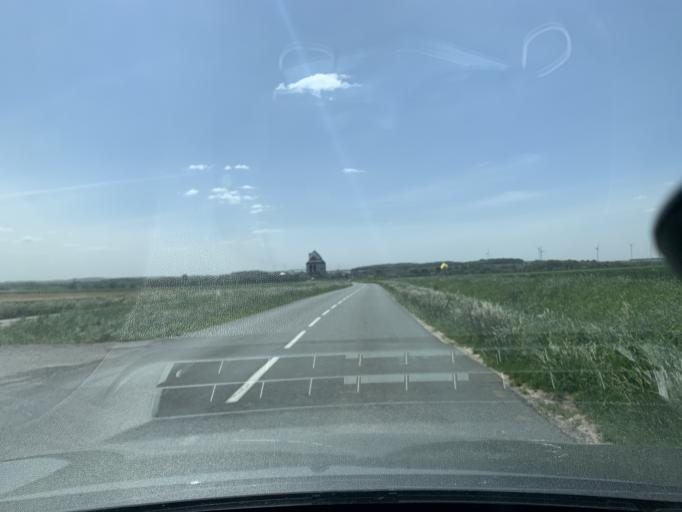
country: FR
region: Nord-Pas-de-Calais
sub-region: Departement du Nord
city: Proville
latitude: 50.1463
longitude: 3.2001
